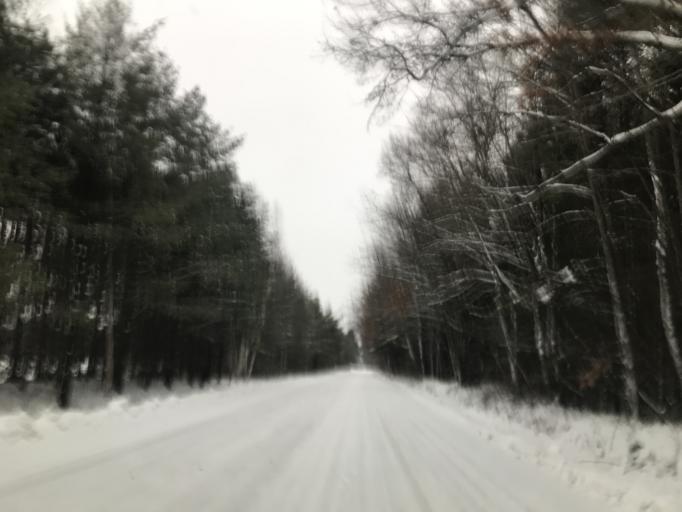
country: US
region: Wisconsin
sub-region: Marinette County
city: Peshtigo
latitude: 45.0491
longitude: -87.7196
